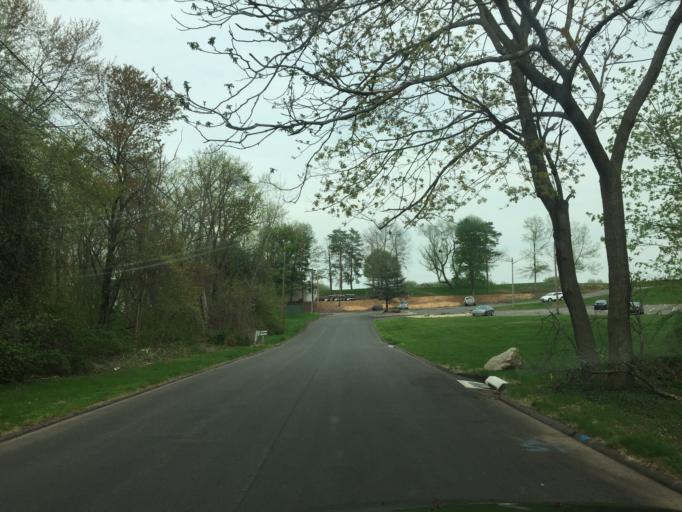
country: US
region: Connecticut
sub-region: Hartford County
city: Newington
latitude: 41.6867
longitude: -72.7416
